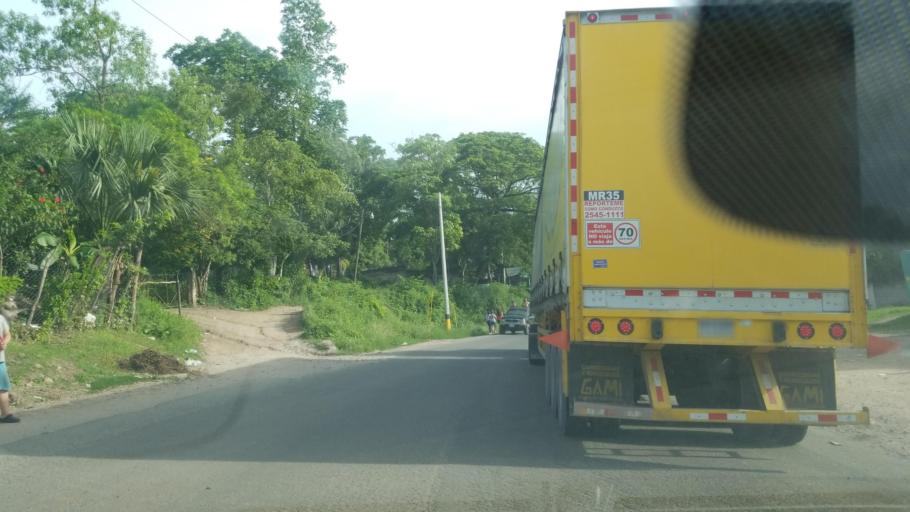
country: HN
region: Santa Barbara
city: Ilama
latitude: 15.0643
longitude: -88.2257
